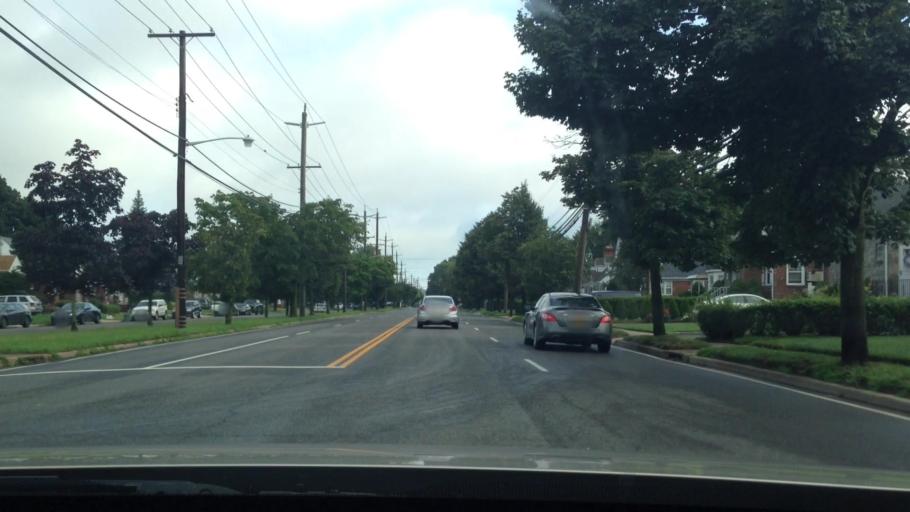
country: US
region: New York
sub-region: Nassau County
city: New Hyde Park
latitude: 40.7423
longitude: -73.6832
